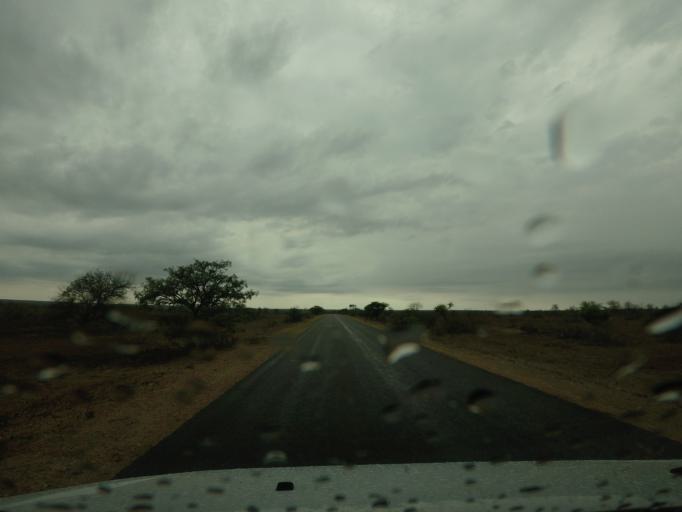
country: ZA
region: Limpopo
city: Thulamahashi
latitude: -24.4746
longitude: 31.4017
